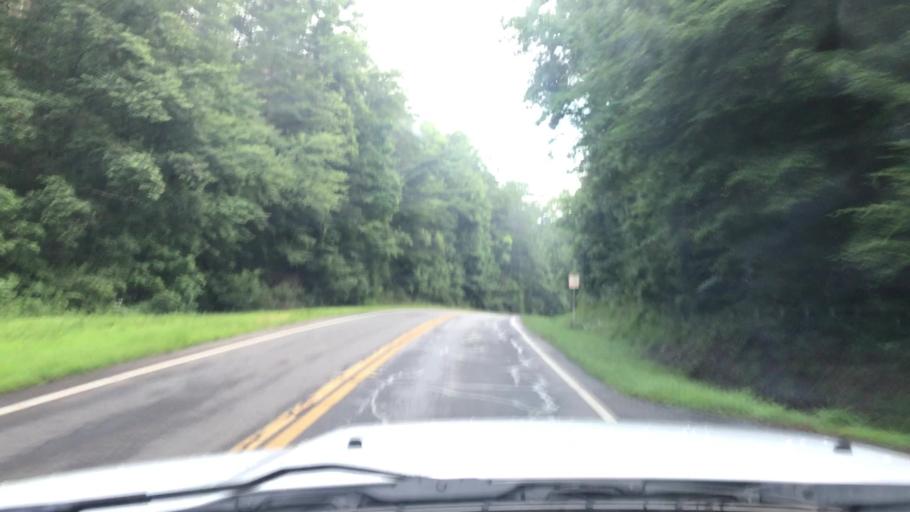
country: US
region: Georgia
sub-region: Fannin County
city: Blue Ridge
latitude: 34.9220
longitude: -84.2711
